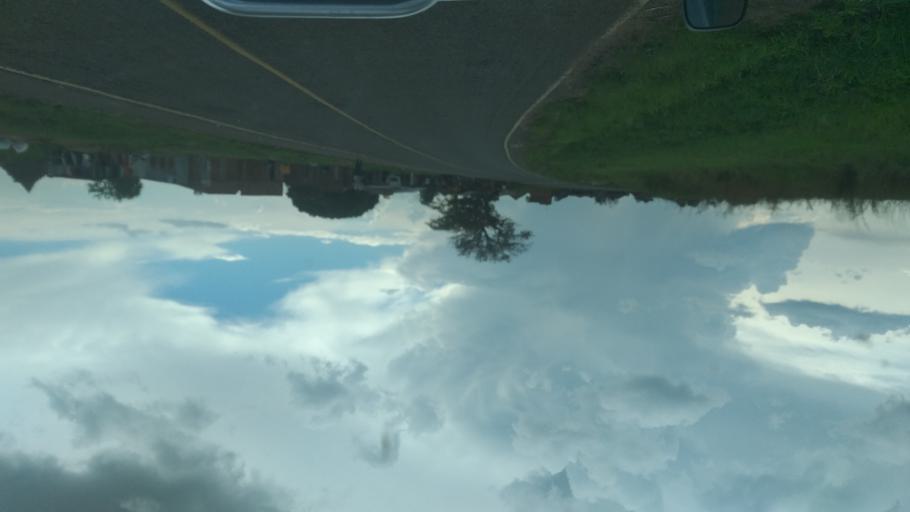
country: UG
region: Northern Region
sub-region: Nwoya District
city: Nwoya
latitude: 2.5797
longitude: 31.7731
